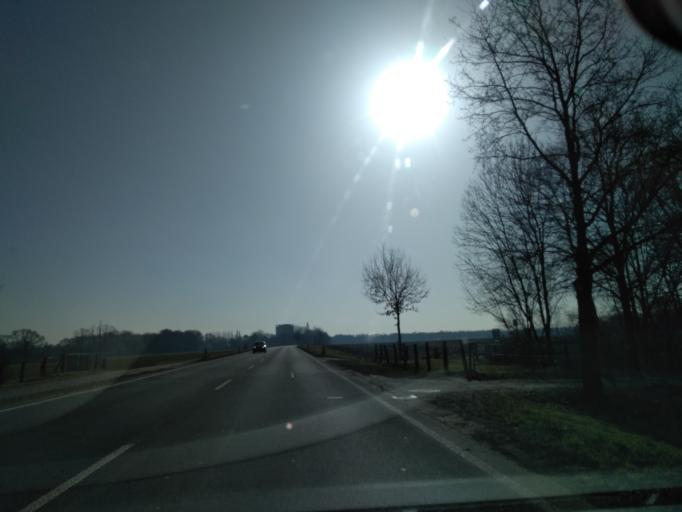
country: DE
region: North Rhine-Westphalia
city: Marl
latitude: 51.6188
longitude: 7.0483
